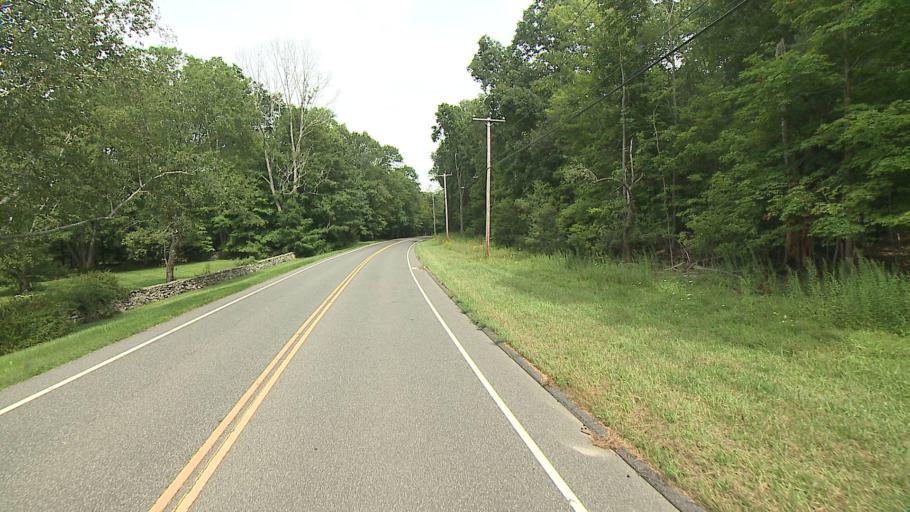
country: US
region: Connecticut
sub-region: Litchfield County
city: New Milford
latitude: 41.5725
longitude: -73.3181
